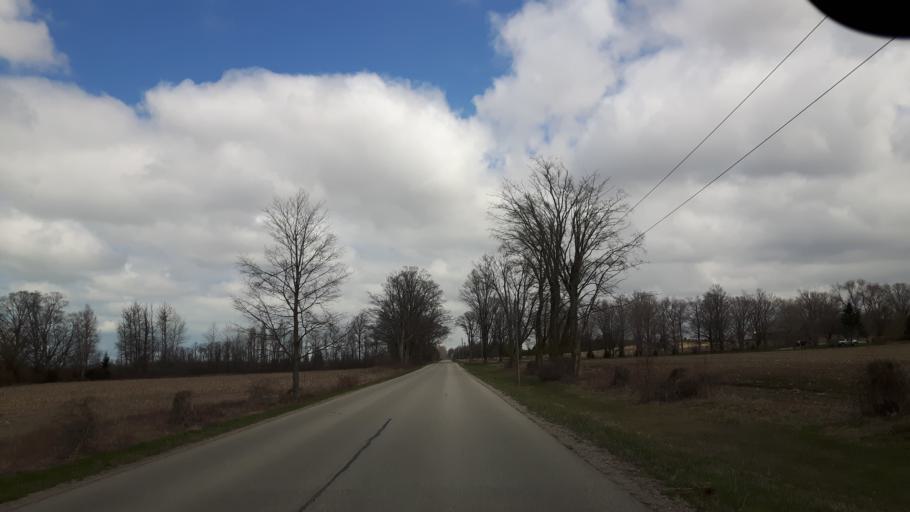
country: CA
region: Ontario
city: Goderich
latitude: 43.6771
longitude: -81.6848
